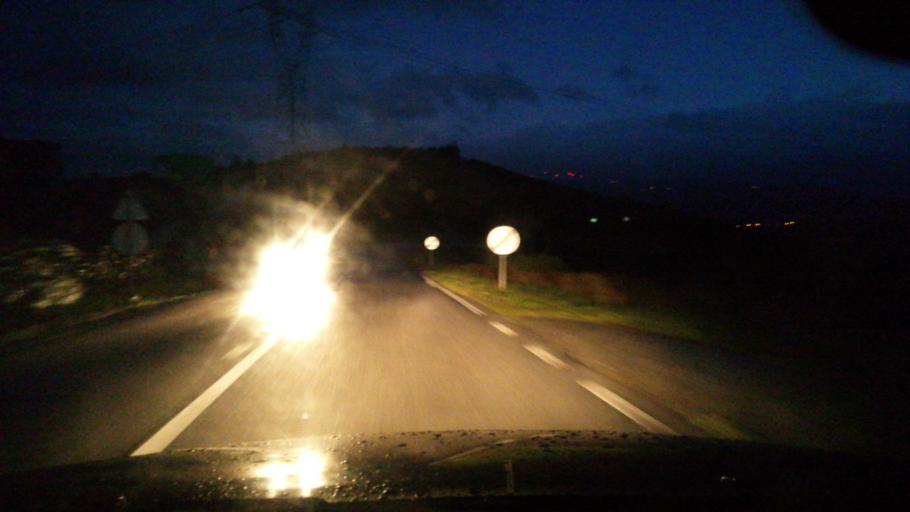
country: PT
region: Viseu
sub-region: Tabuaco
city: Tabuaco
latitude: 41.1245
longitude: -7.5156
